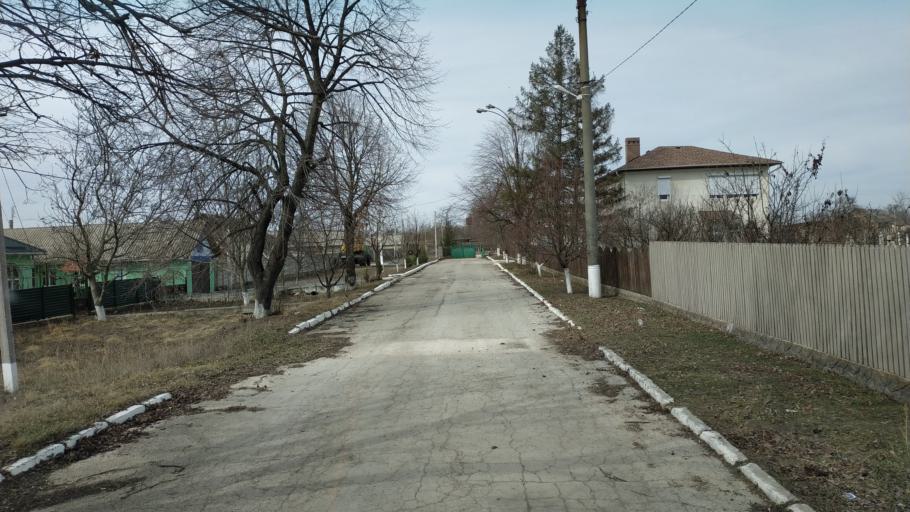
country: MD
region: Hincesti
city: Dancu
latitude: 46.8607
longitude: 28.2490
